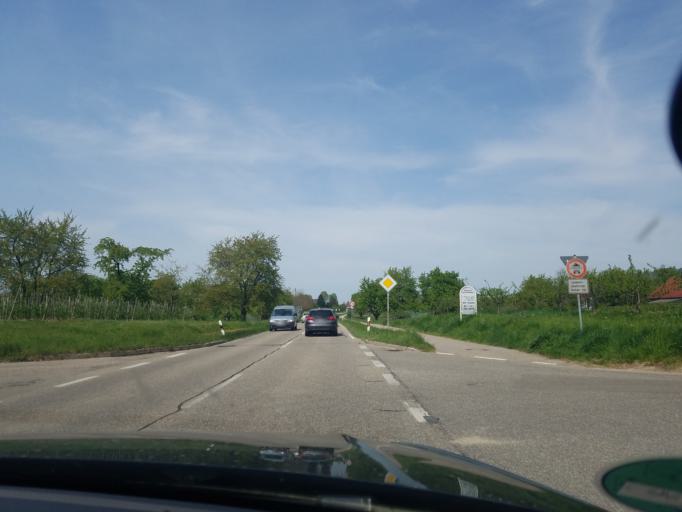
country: DE
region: Baden-Wuerttemberg
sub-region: Freiburg Region
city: Haslach
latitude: 48.5573
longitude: 8.0596
